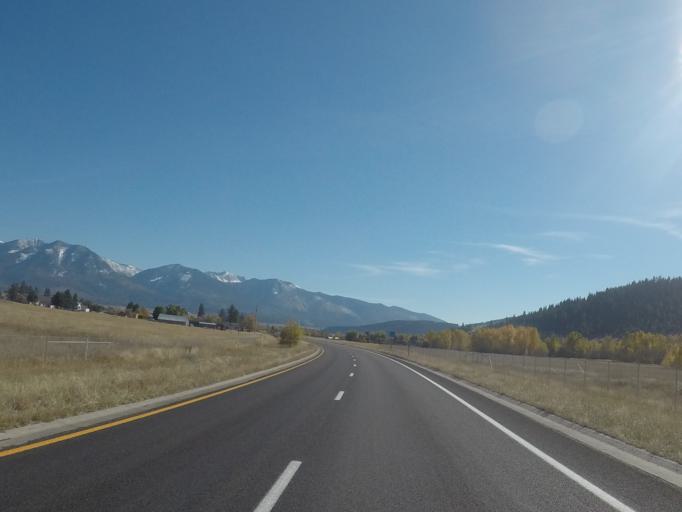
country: US
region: Montana
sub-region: Missoula County
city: Frenchtown
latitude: 47.1657
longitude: -114.0910
